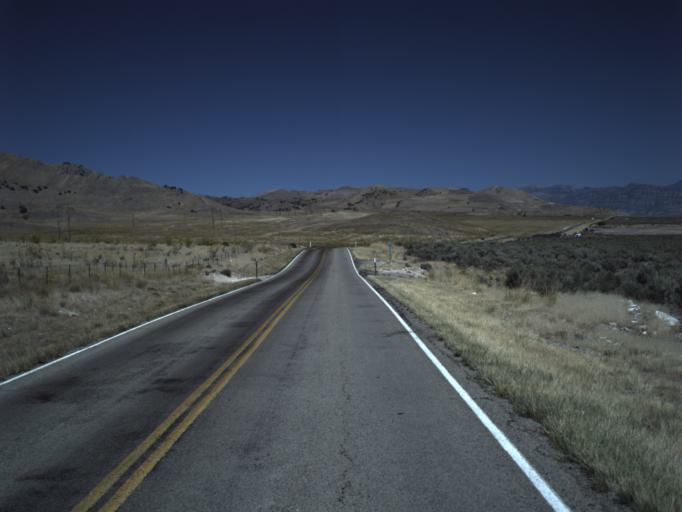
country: US
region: Utah
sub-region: Utah County
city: Saratoga Springs
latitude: 40.1940
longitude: -111.9050
